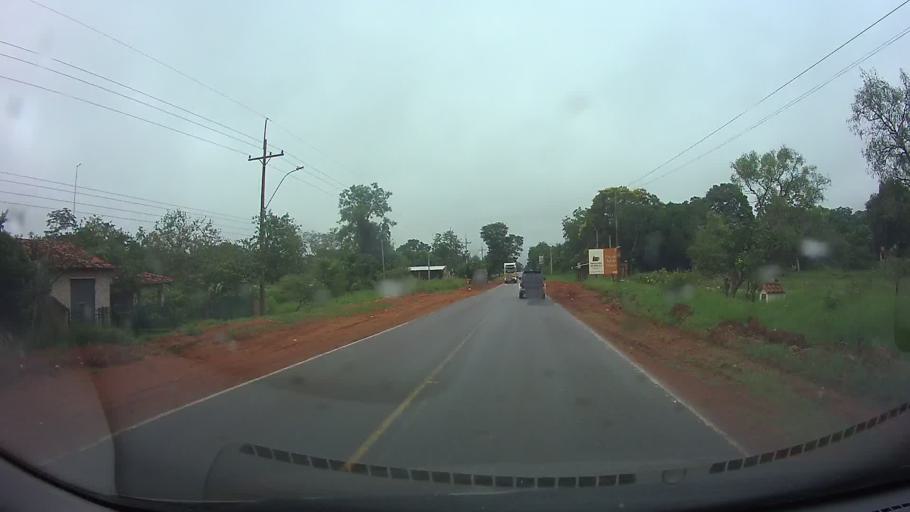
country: PY
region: Central
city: Itaugua
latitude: -25.4239
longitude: -57.3636
